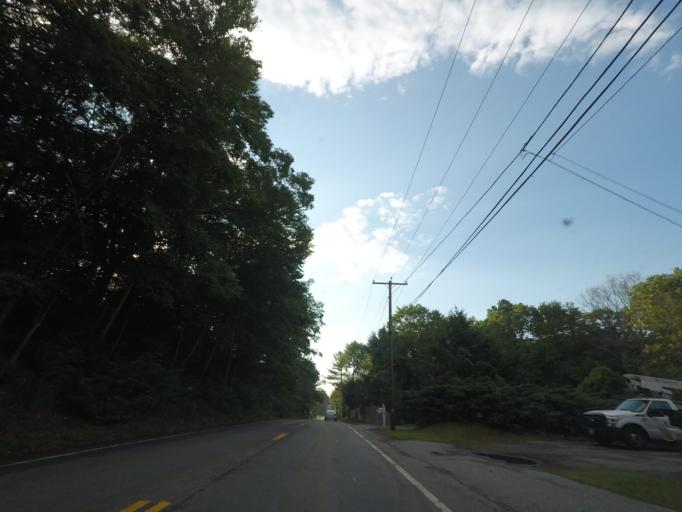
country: US
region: Connecticut
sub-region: Windham County
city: Quinebaug
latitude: 42.0362
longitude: -71.9692
